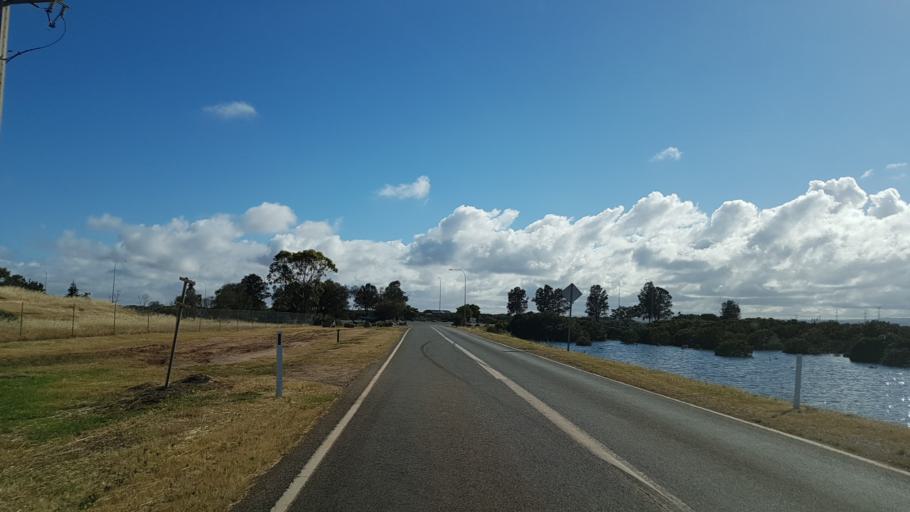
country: AU
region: South Australia
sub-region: Port Adelaide Enfield
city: Birkenhead
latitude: -34.8068
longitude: 138.5389
